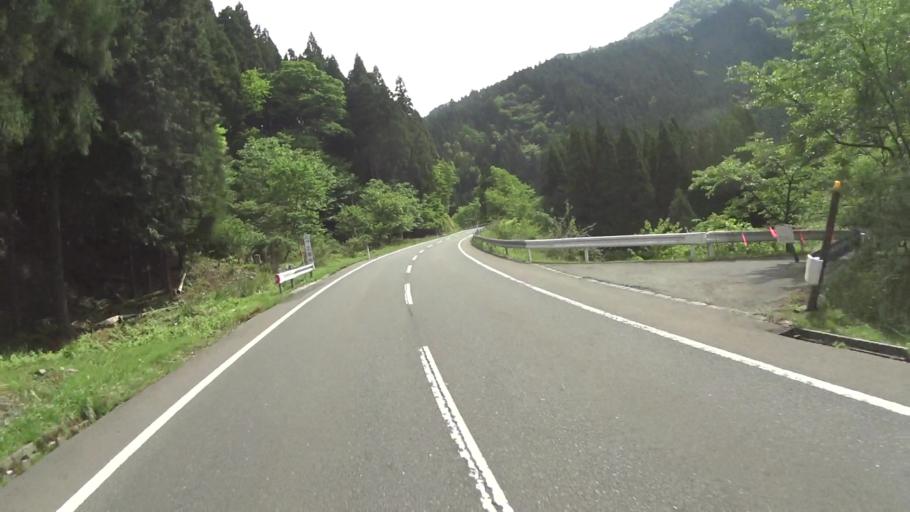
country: JP
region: Shiga Prefecture
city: Kitahama
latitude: 35.2264
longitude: 135.8622
